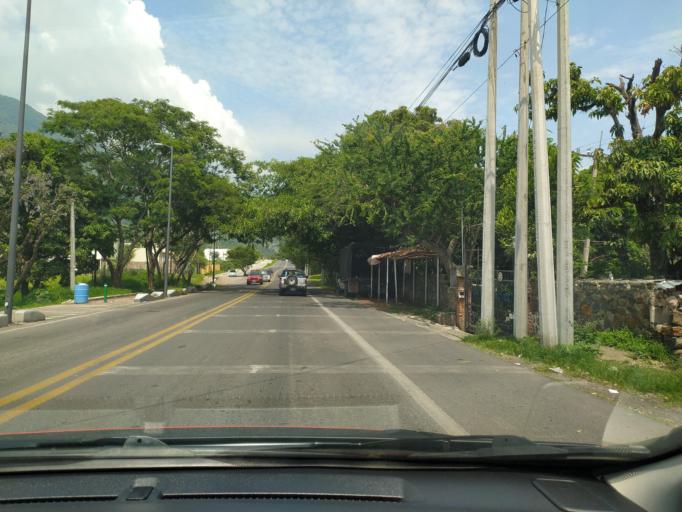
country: MX
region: Jalisco
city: Jocotepec
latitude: 20.2937
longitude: -103.3899
